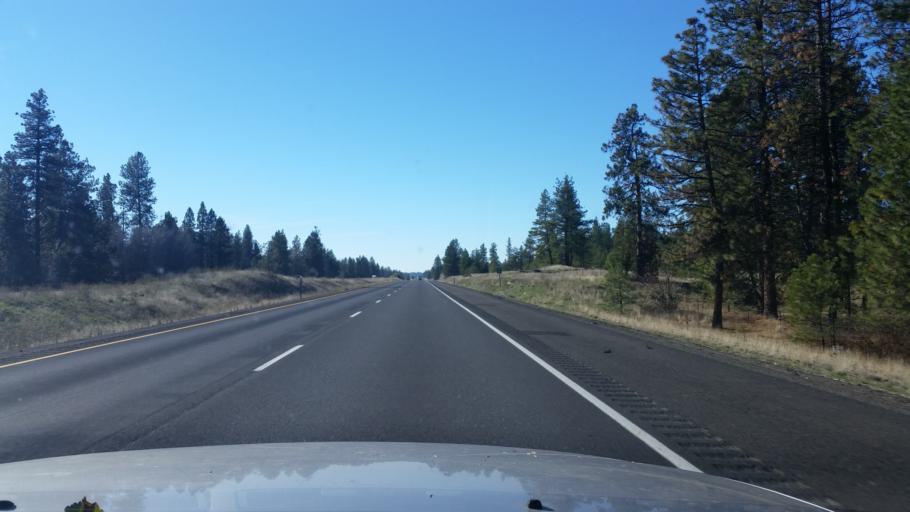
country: US
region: Washington
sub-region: Spokane County
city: Medical Lake
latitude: 47.4663
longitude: -117.7470
